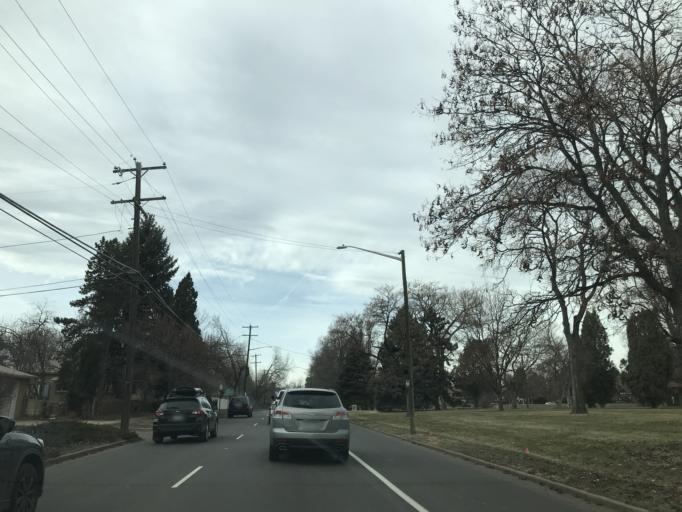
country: US
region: Colorado
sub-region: Denver County
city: Denver
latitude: 39.7292
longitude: -104.9558
